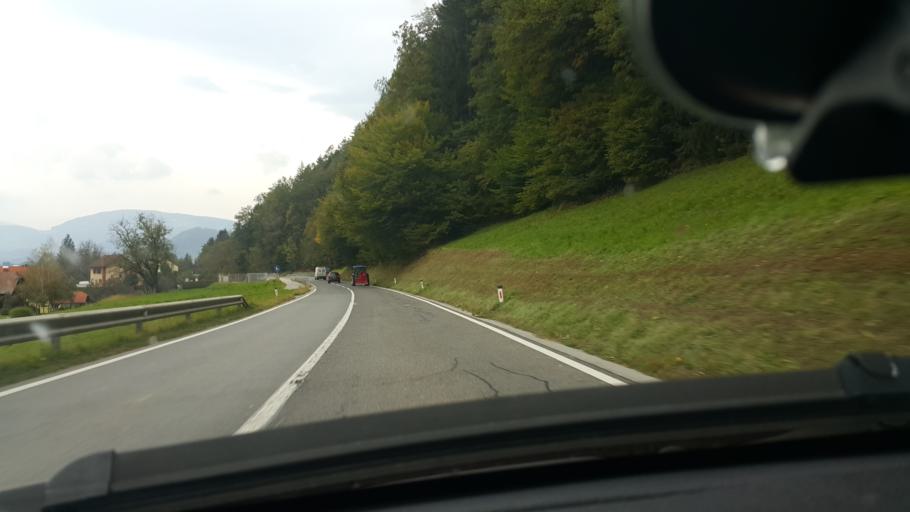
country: SI
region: Radlje ob Dravi
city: Radlje ob Dravi
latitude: 46.5967
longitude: 15.2672
